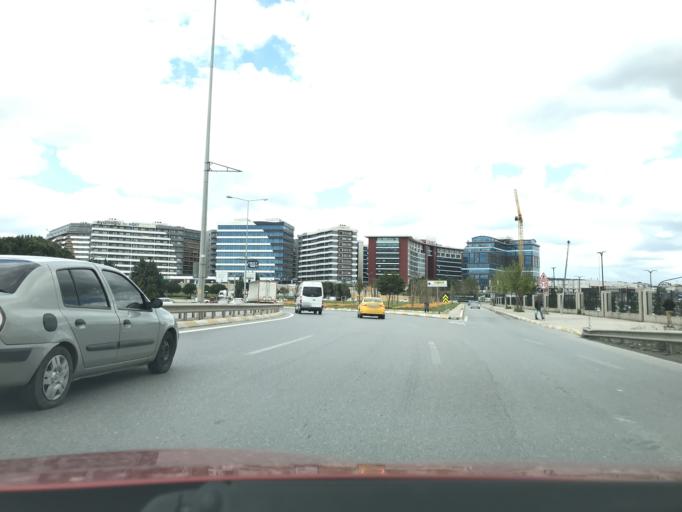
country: TR
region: Istanbul
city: Sultanbeyli
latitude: 40.9234
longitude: 29.3130
